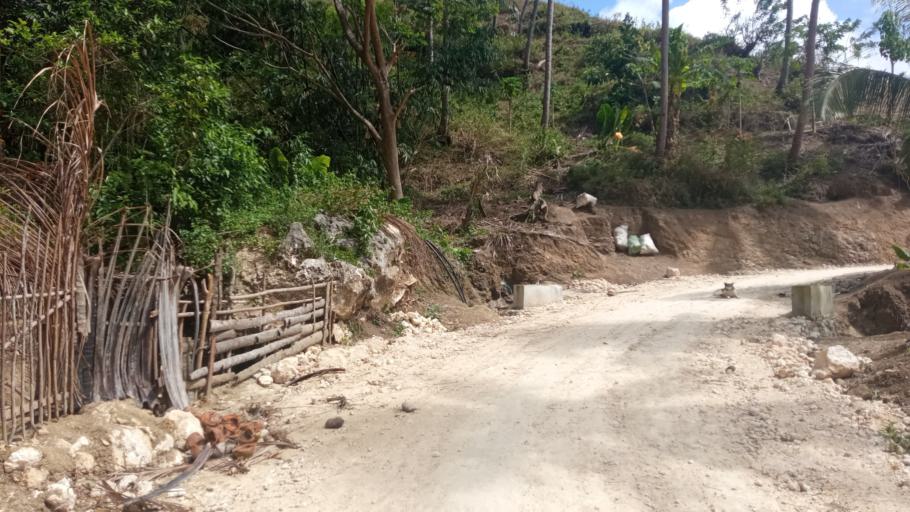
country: PH
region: Central Visayas
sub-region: Province of Siquijor
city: Lazi
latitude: 9.1557
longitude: 123.5787
